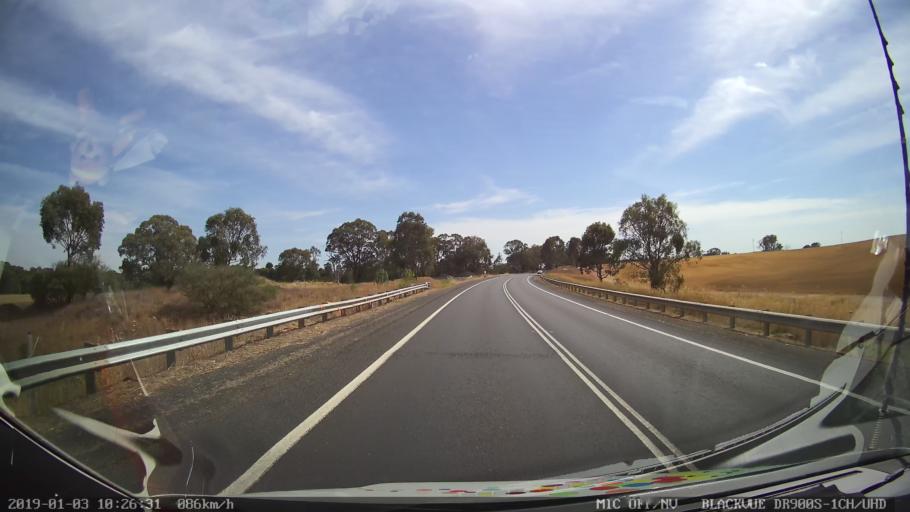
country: AU
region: New South Wales
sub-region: Young
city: Young
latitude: -34.4116
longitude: 148.2499
